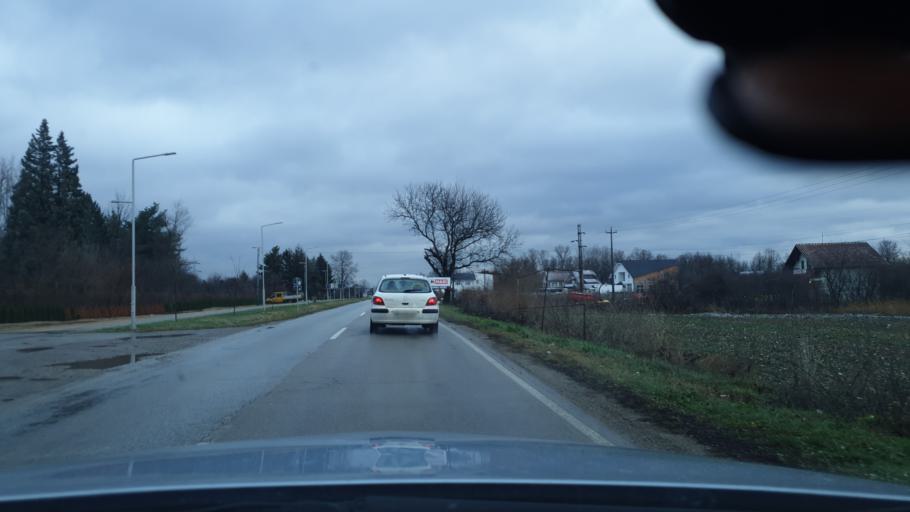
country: RS
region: Central Serbia
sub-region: Branicevski Okrug
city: Petrovac
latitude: 44.3961
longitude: 21.4041
